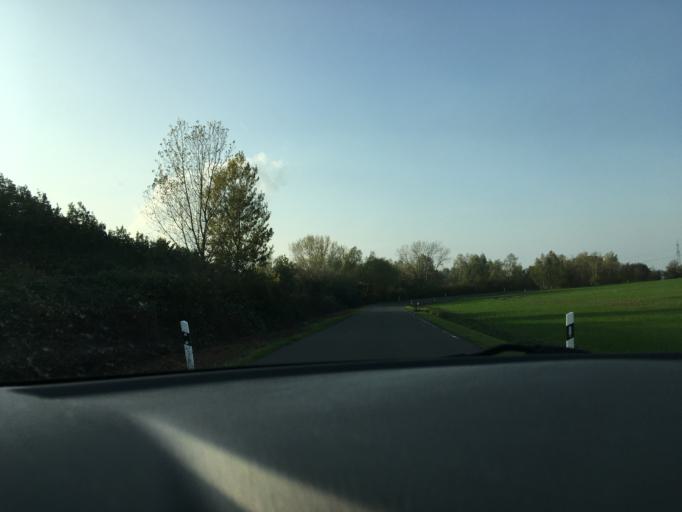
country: DE
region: Saxony
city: Neukieritzsch
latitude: 51.1810
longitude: 12.4395
